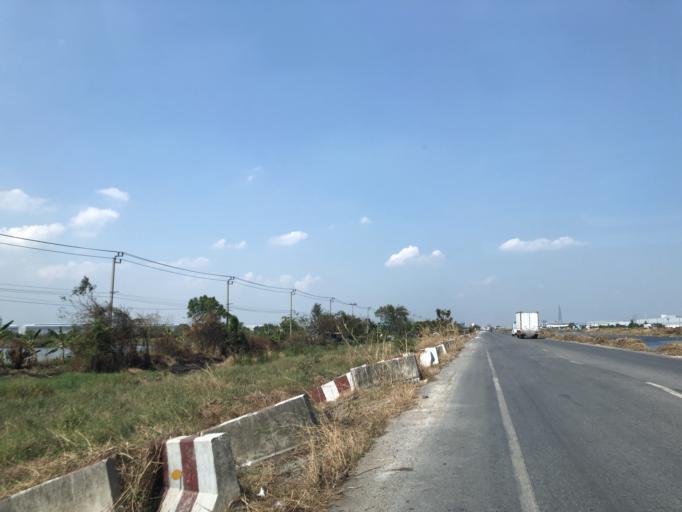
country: TH
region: Samut Prakan
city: Bang Bo District
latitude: 13.5668
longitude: 100.7554
